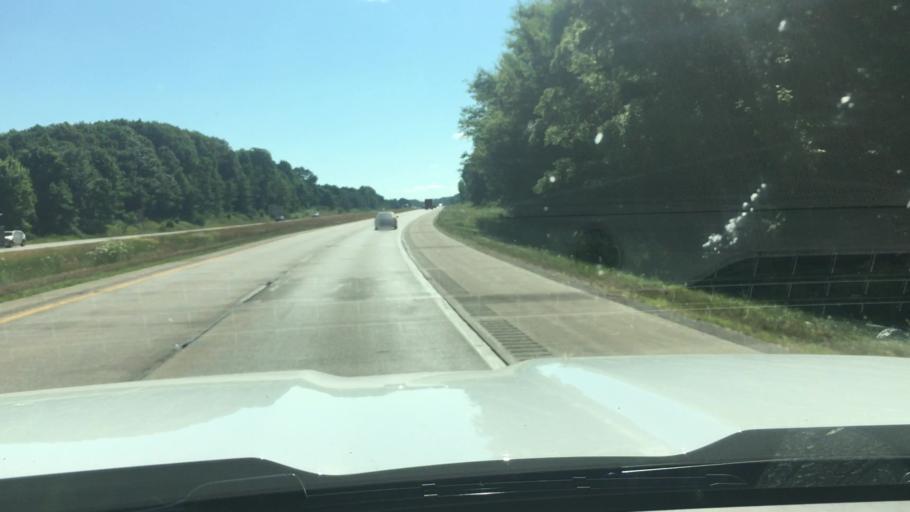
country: US
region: Michigan
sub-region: Clinton County
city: DeWitt
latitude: 42.8072
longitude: -84.6227
